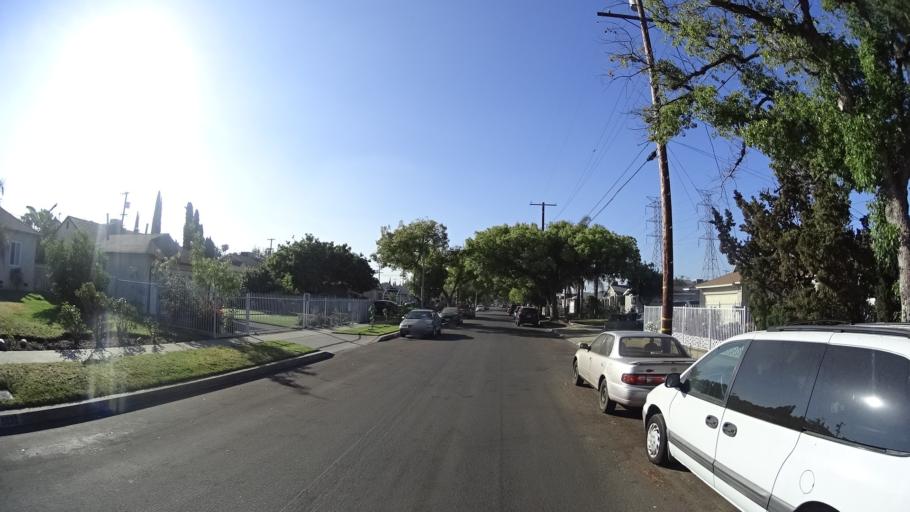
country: US
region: California
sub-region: Los Angeles County
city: Van Nuys
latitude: 34.2300
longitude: -118.4237
